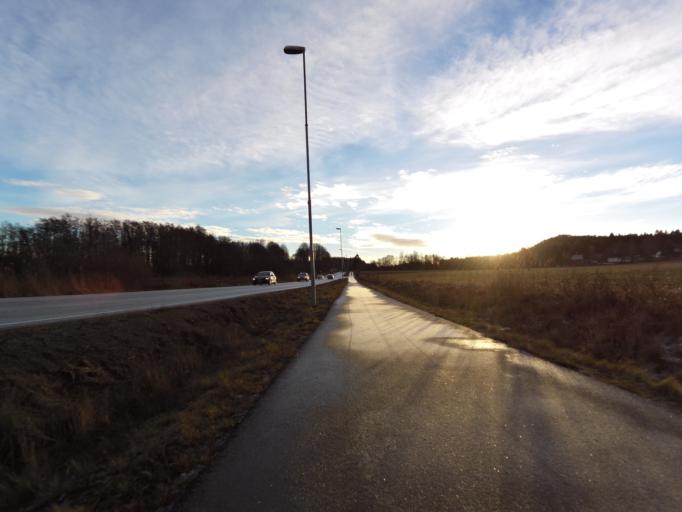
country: NO
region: Ostfold
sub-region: Fredrikstad
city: Fredrikstad
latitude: 59.2381
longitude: 10.9011
